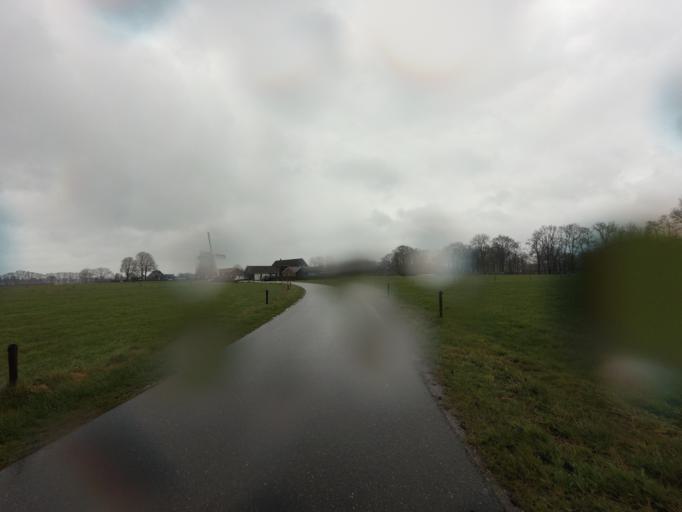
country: NL
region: Gelderland
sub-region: Gemeente Epe
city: Vaassen
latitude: 52.2608
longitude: 5.9704
